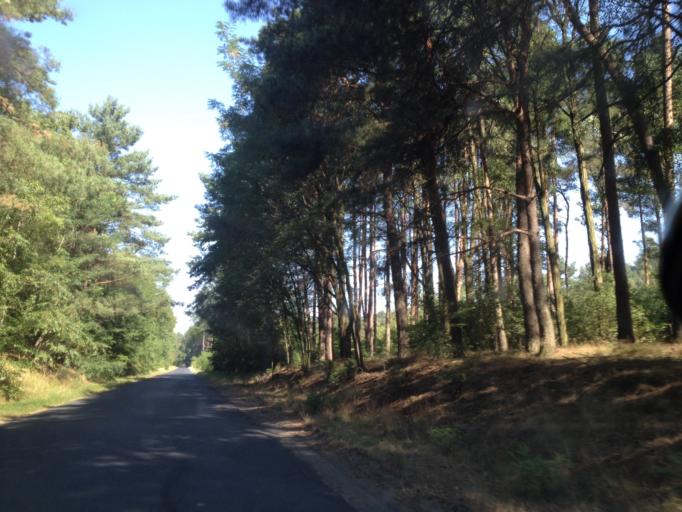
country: PL
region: Greater Poland Voivodeship
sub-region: Powiat sredzki
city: Zaniemysl
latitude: 52.1218
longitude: 17.1120
